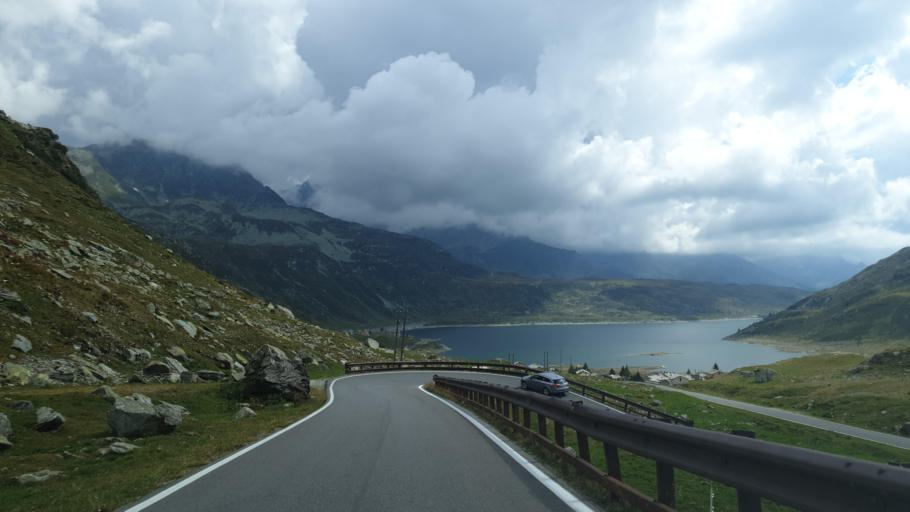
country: IT
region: Lombardy
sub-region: Provincia di Sondrio
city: Campodolcino
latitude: 46.4929
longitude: 9.3316
